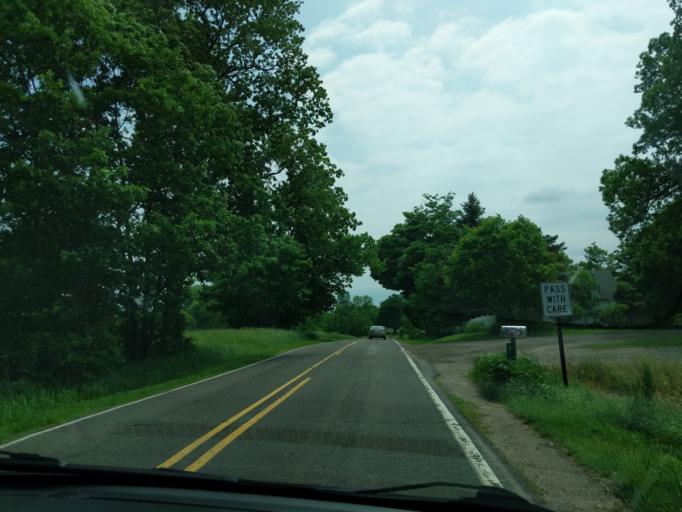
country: US
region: Michigan
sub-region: Ingham County
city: Williamston
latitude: 42.6935
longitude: -84.2451
